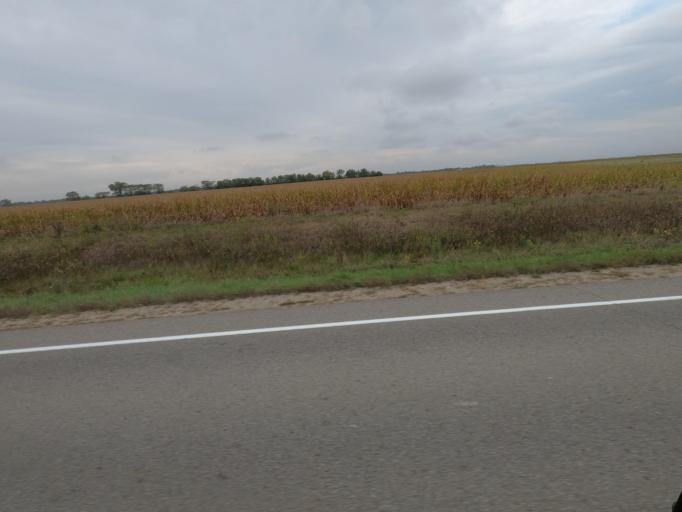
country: US
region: Iowa
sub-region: Van Buren County
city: Keosauqua
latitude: 40.8135
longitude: -91.8585
